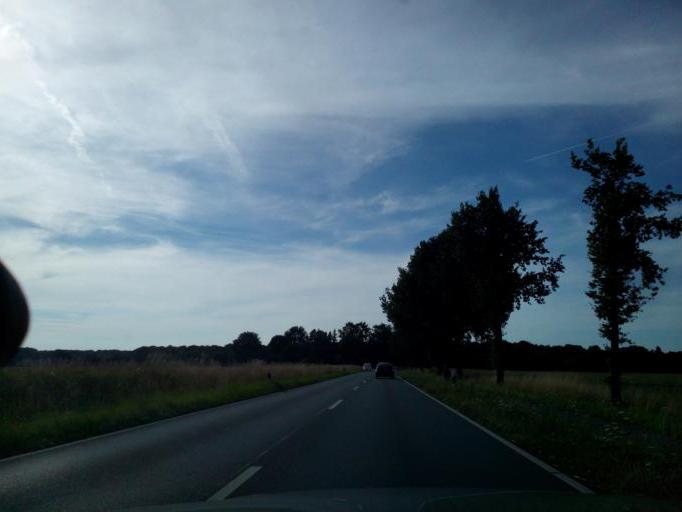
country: DE
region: North Rhine-Westphalia
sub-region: Regierungsbezirk Munster
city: Muenster
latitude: 51.9432
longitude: 7.5671
